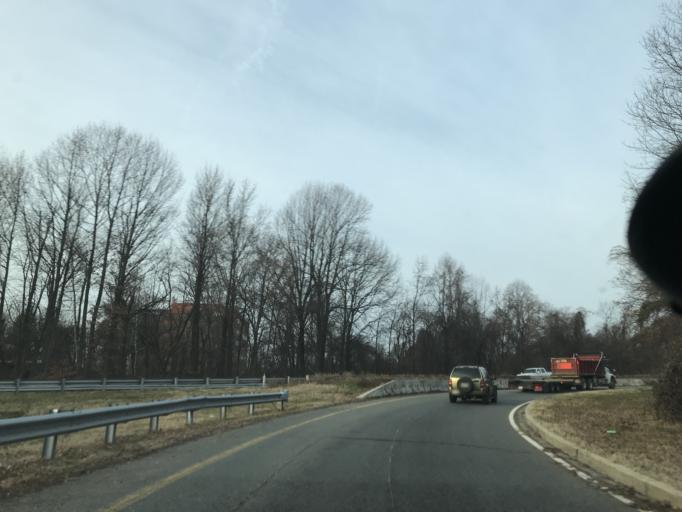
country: US
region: Maryland
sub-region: Prince George's County
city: Glenarden
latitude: 38.9159
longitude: -76.8523
